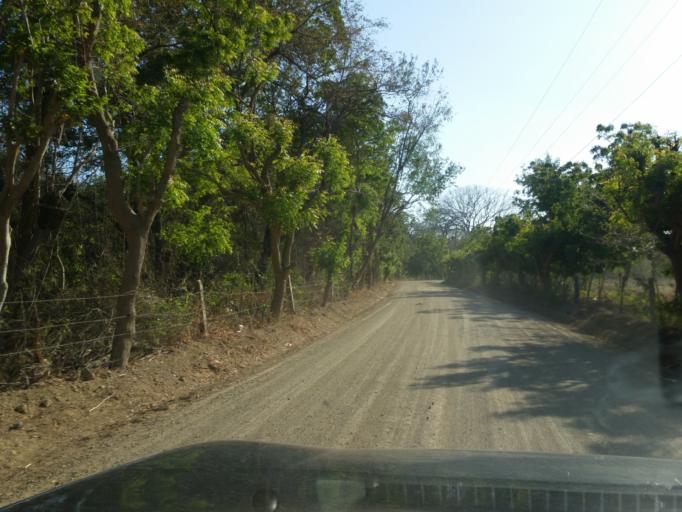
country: NI
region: Rivas
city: Tola
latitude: 11.4227
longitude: -86.0318
